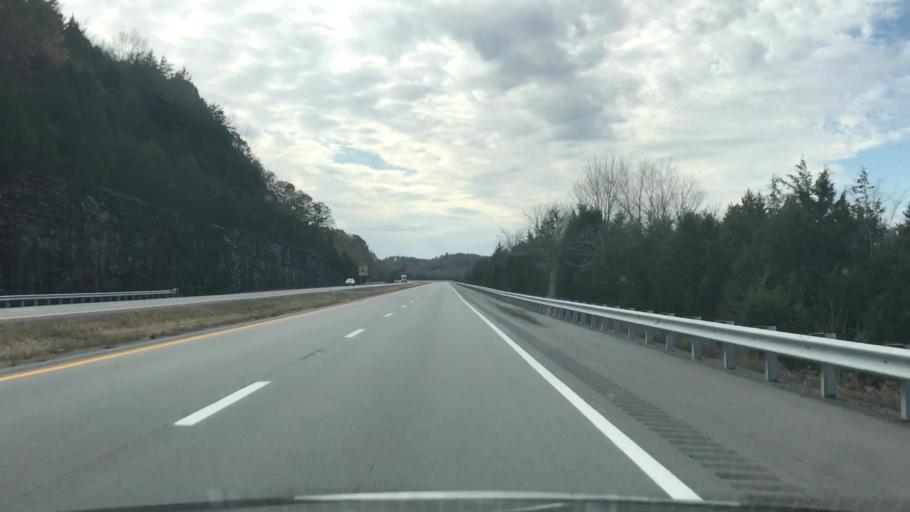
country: US
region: Kentucky
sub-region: Adair County
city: Columbia
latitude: 37.0549
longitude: -85.4336
